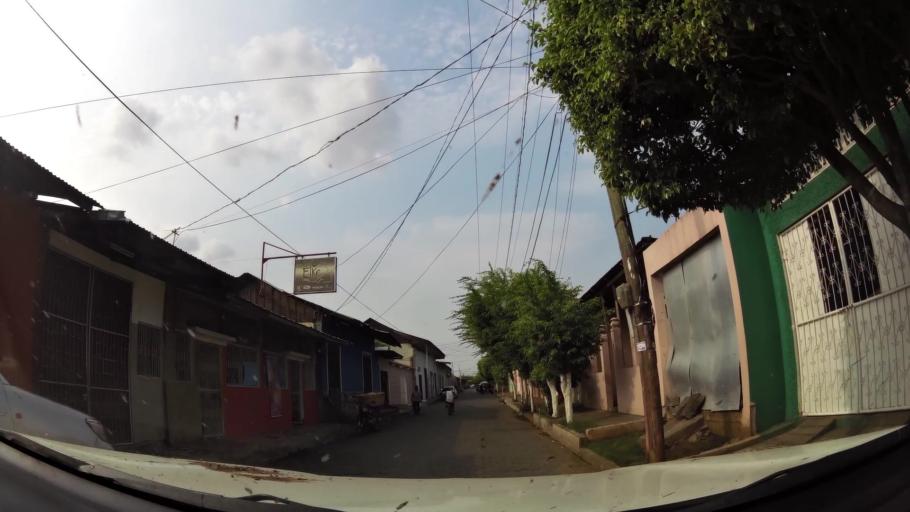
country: NI
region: Masaya
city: Masaya
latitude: 11.9704
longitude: -86.0926
